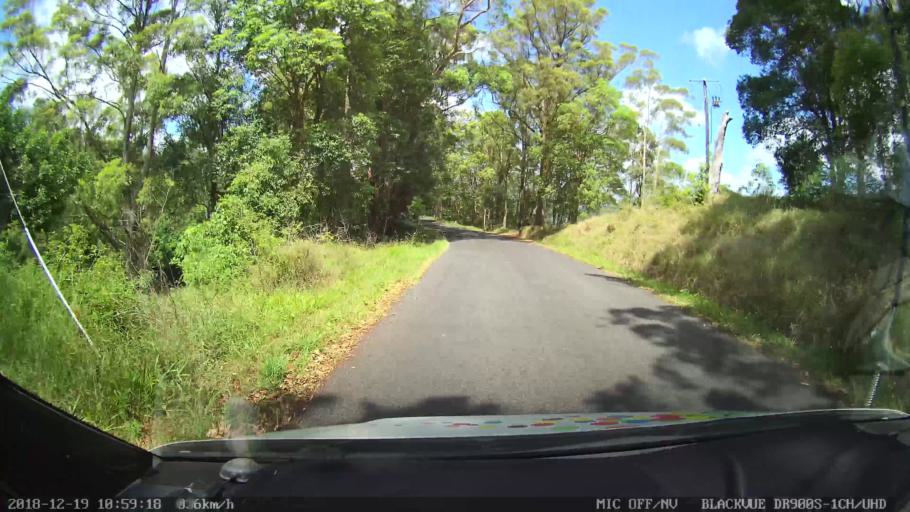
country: AU
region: New South Wales
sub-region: Lismore Municipality
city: Nimbin
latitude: -28.5960
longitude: 153.2630
